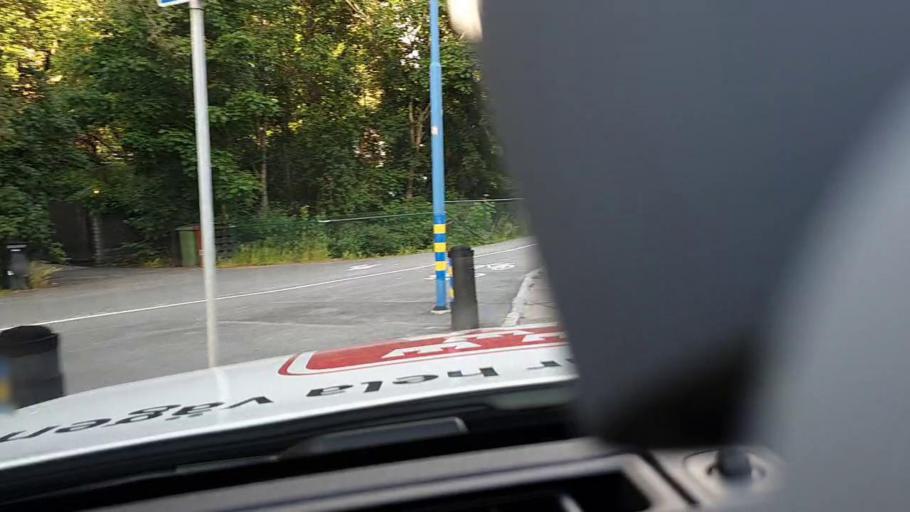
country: SE
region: Stockholm
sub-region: Huddinge Kommun
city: Huddinge
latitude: 59.2443
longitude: 17.9753
